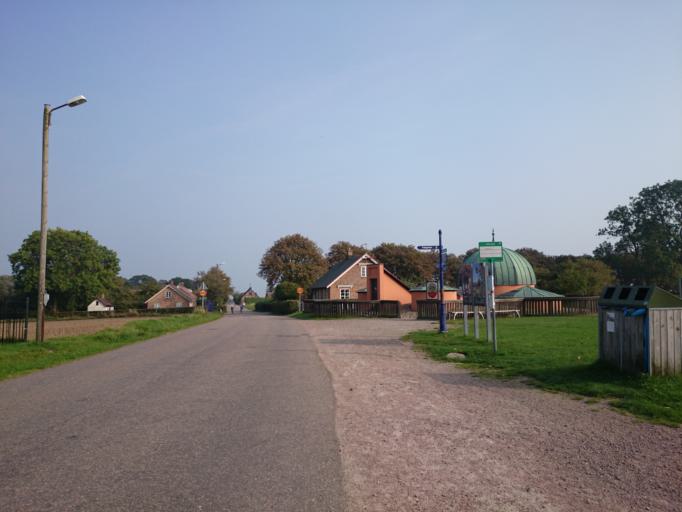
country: SE
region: Skane
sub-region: Helsingborg
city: Rydeback
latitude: 55.9071
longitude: 12.6967
